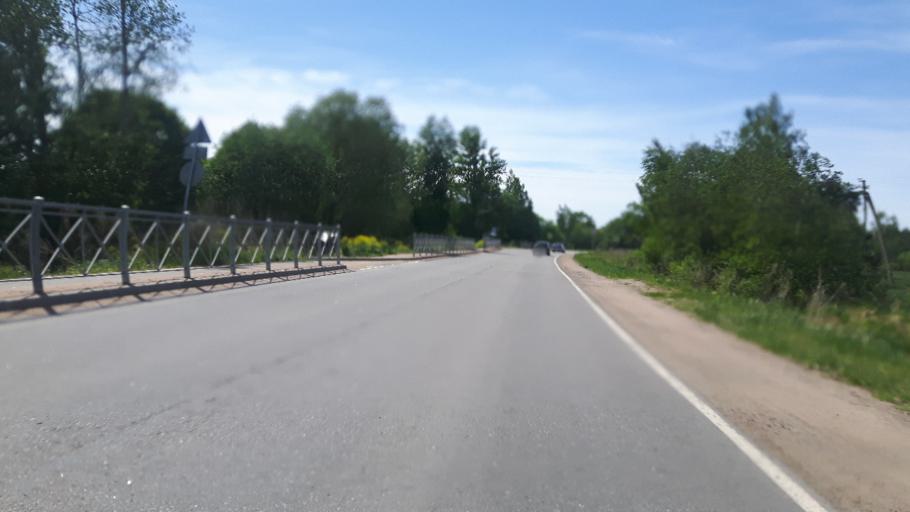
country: RU
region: Leningrad
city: Ust'-Luga
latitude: 59.5712
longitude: 28.1687
